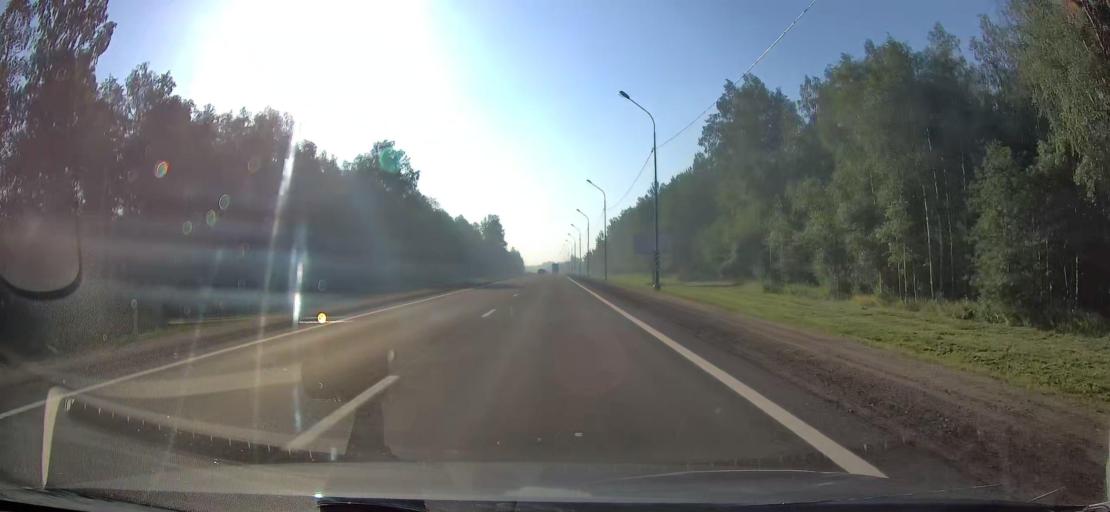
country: RU
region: Leningrad
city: Sinyavino
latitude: 59.8923
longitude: 31.1467
